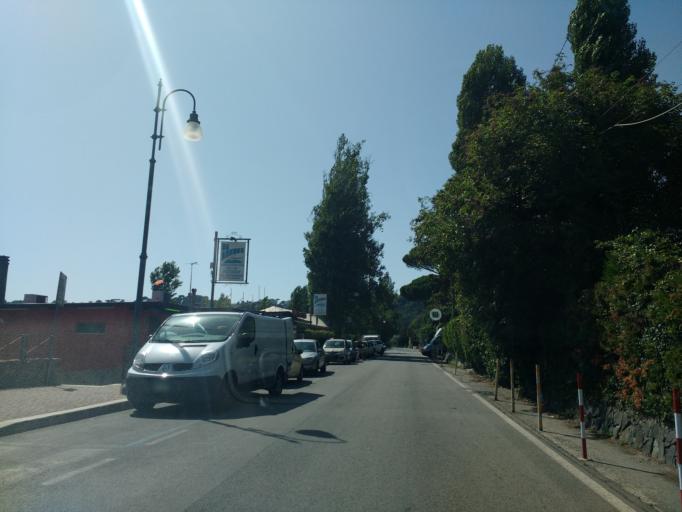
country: IT
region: Latium
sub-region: Citta metropolitana di Roma Capitale
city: Castel Gandolfo
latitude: 41.7603
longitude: 12.6654
